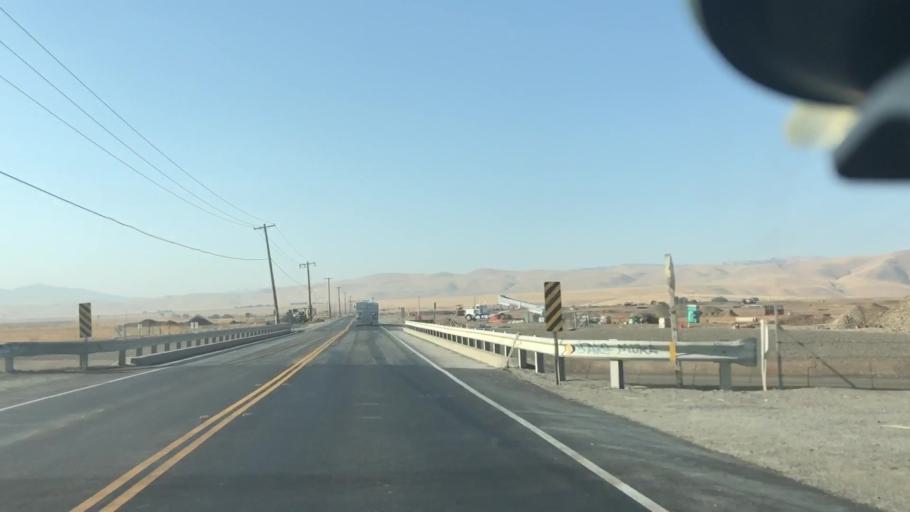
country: US
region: California
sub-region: San Joaquin County
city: Tracy
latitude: 37.6805
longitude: -121.4528
